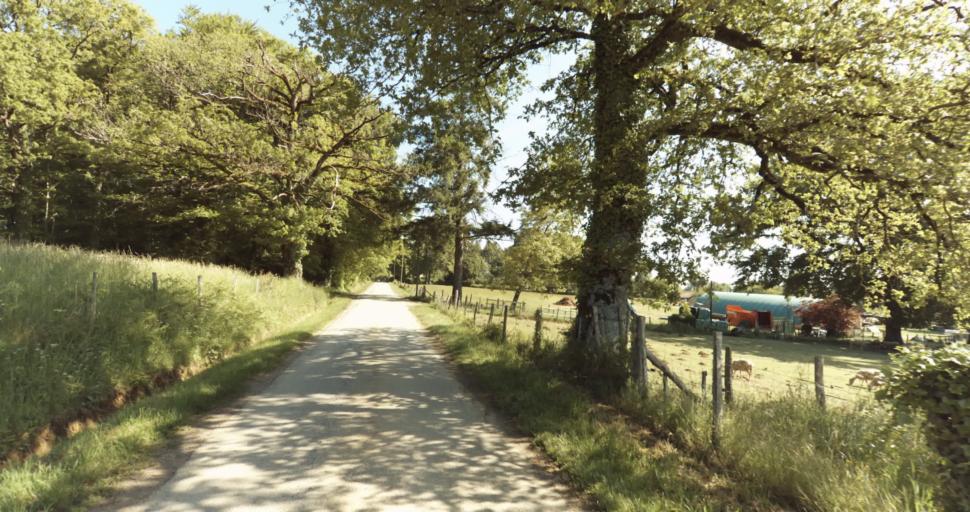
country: FR
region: Limousin
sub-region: Departement de la Haute-Vienne
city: Solignac
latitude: 45.7170
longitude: 1.2662
